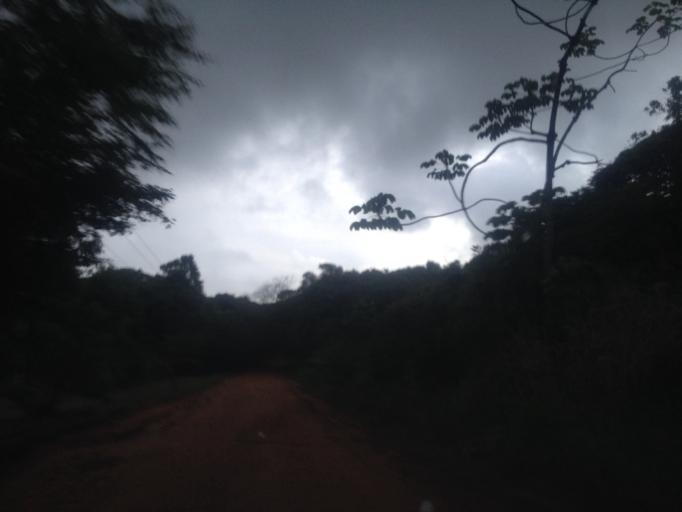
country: BR
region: Bahia
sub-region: Mata De Sao Joao
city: Mata de Sao Joao
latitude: -12.5717
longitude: -38.0232
